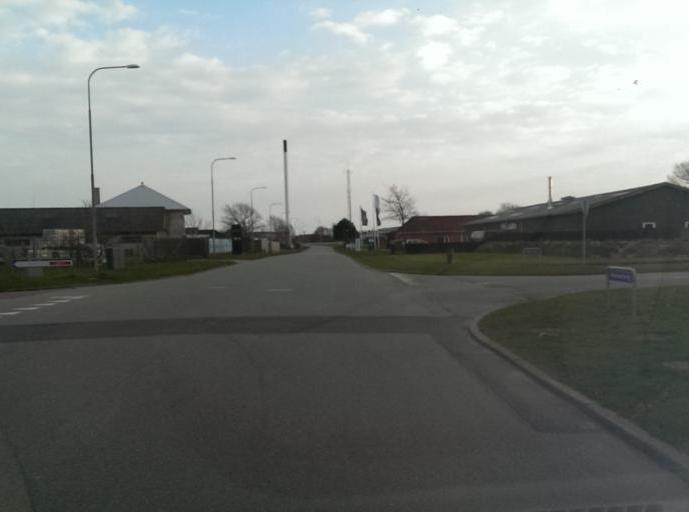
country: DK
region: South Denmark
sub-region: Esbjerg Kommune
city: Esbjerg
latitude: 55.5068
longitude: 8.4095
